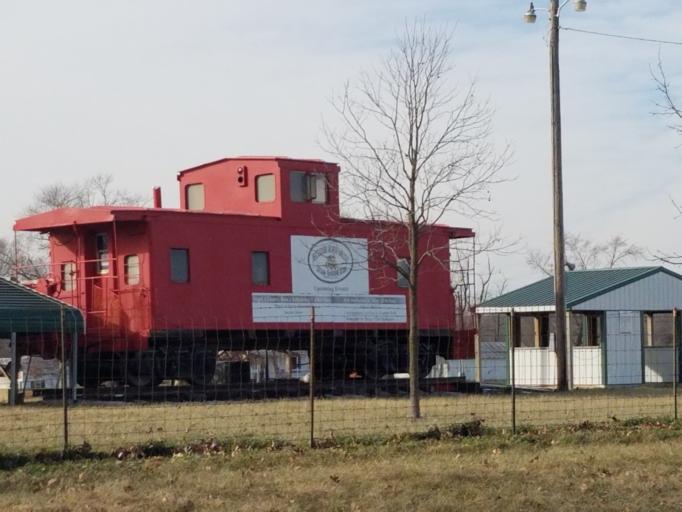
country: US
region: Missouri
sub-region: Cooper County
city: Boonville
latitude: 38.9367
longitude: -92.5953
